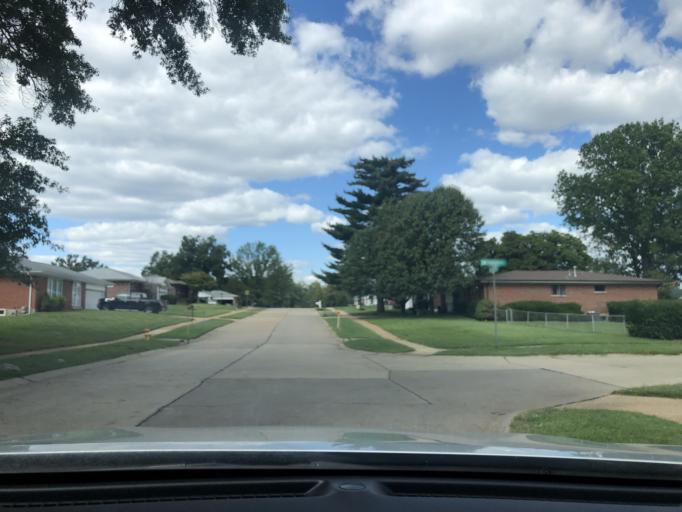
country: US
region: Missouri
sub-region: Saint Louis County
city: Concord
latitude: 38.4991
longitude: -90.3573
